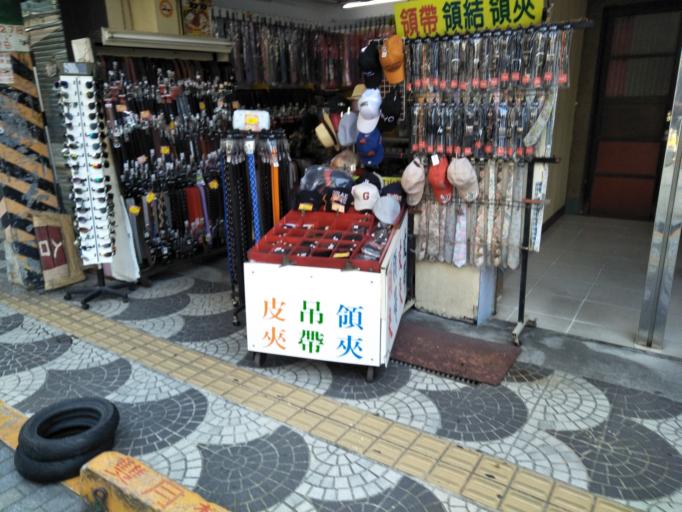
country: TW
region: Taiwan
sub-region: Changhua
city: Chang-hua
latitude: 24.0768
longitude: 120.5405
